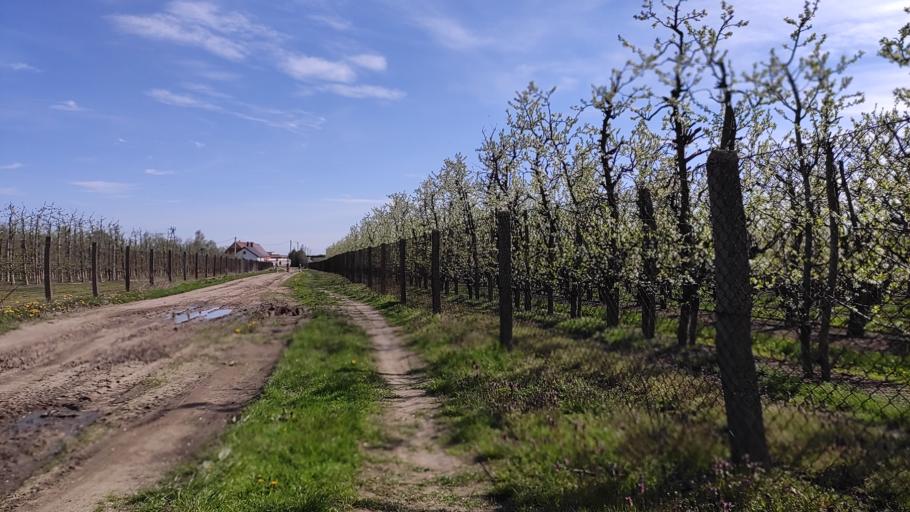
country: PL
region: Greater Poland Voivodeship
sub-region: Powiat poznanski
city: Kostrzyn
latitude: 52.4001
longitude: 17.1770
